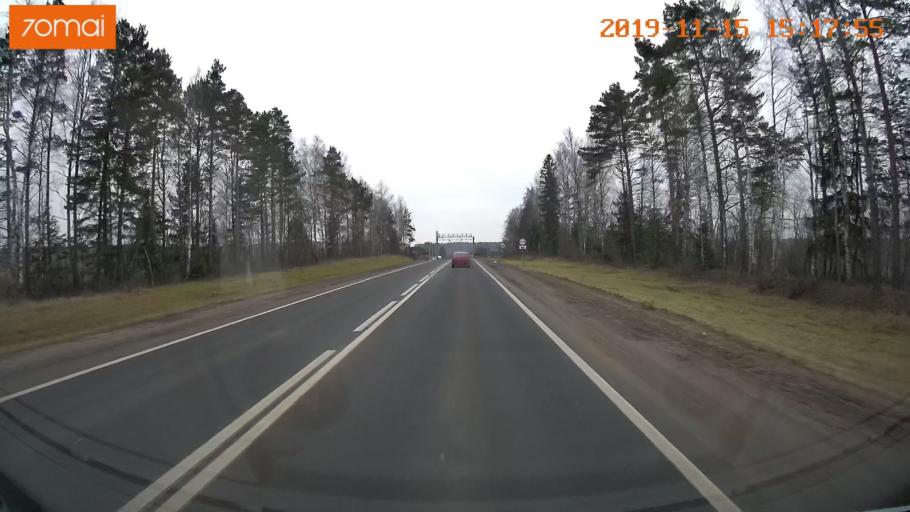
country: RU
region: Jaroslavl
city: Danilov
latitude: 58.2540
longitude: 40.1807
